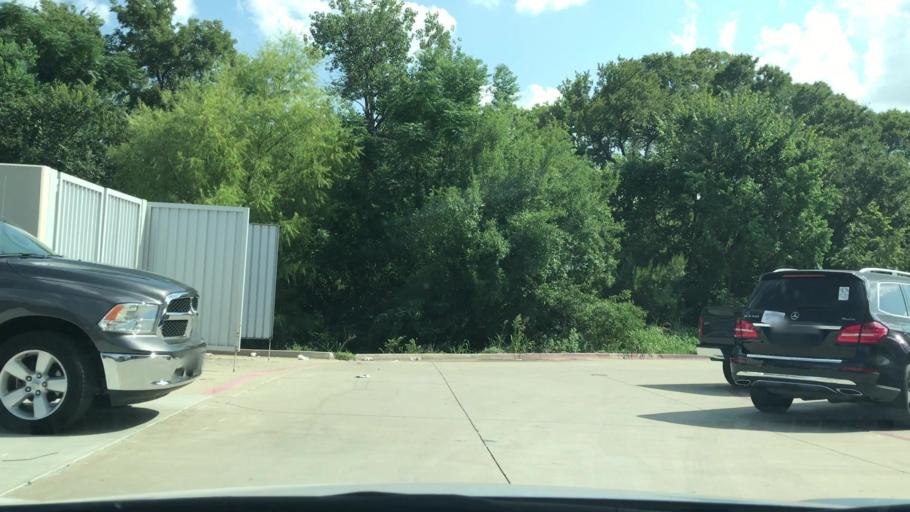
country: US
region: Texas
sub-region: Dallas County
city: Addison
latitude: 32.9712
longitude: -96.8438
